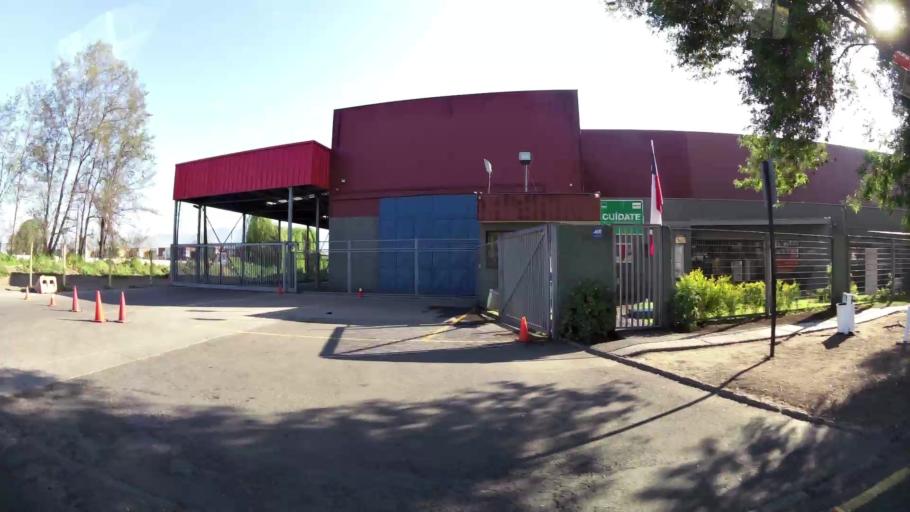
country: CL
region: Santiago Metropolitan
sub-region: Provincia de Chacabuco
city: Chicureo Abajo
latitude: -33.3683
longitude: -70.6649
